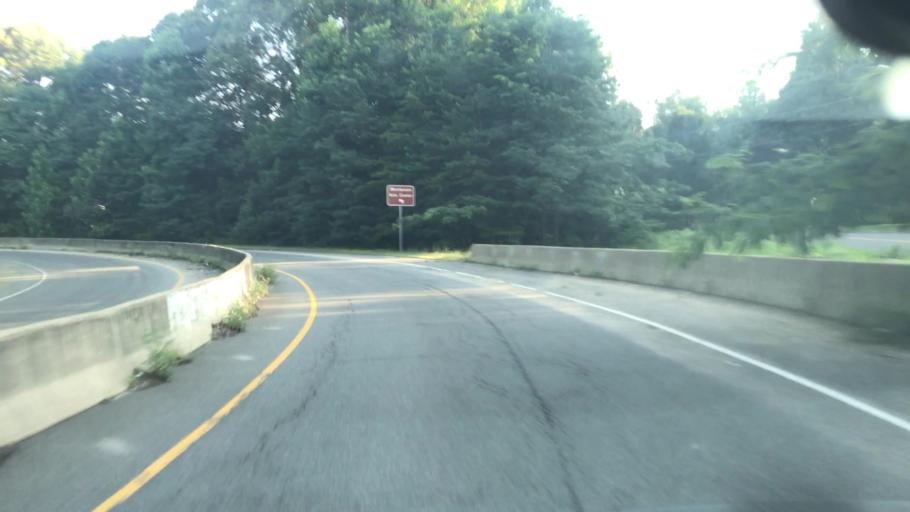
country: US
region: Virginia
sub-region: Fairfax County
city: Fairfax Station
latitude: 38.7894
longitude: -77.3246
